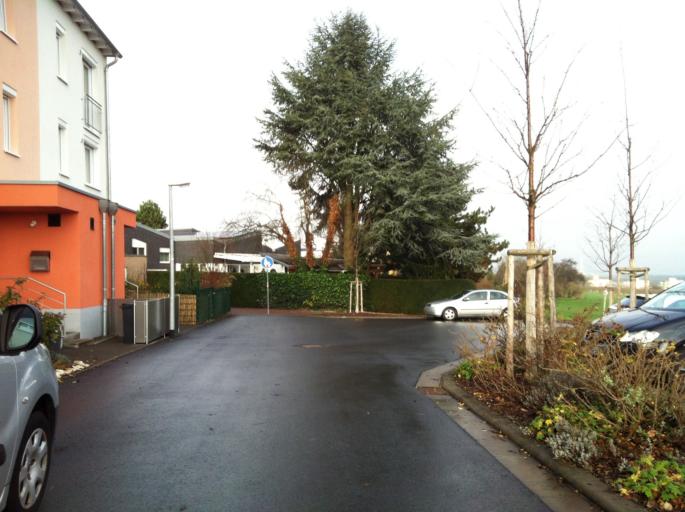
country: DE
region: Rheinland-Pfalz
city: Budenheim
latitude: 49.9889
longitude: 8.1863
